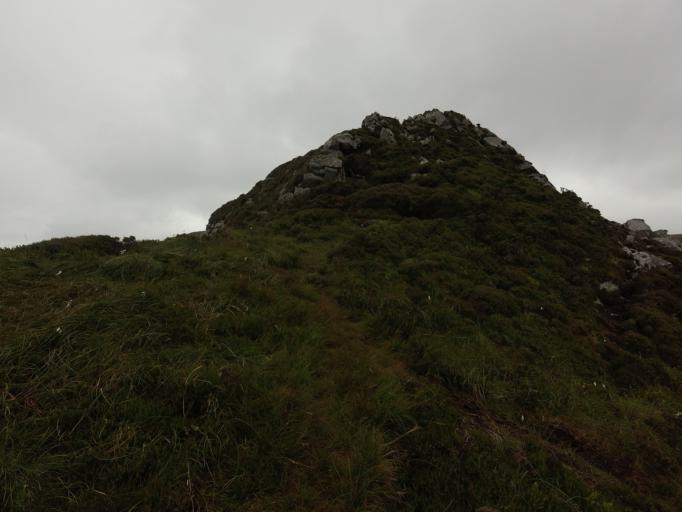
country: IE
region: Ulster
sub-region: County Donegal
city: Killybegs
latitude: 54.6440
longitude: -8.6876
